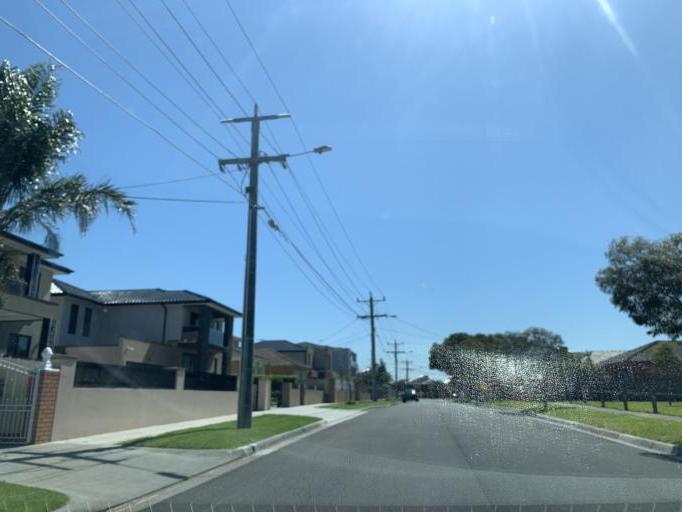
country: AU
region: Victoria
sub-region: Greater Dandenong
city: Dandenong
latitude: -38.0013
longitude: 145.2102
